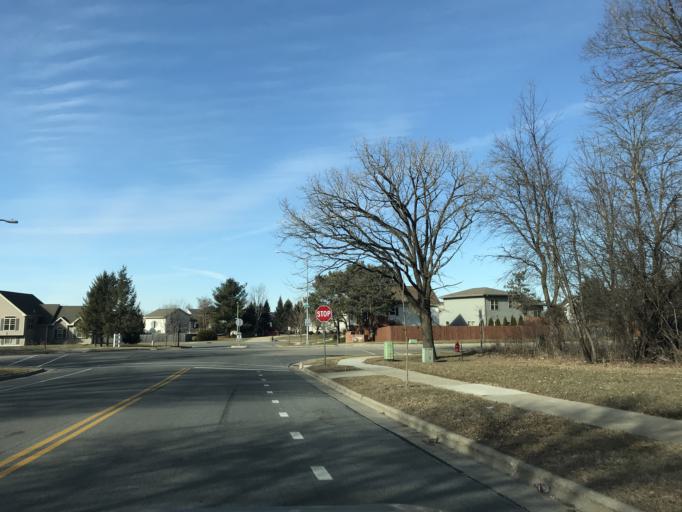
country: US
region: Wisconsin
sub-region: Dane County
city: Maple Bluff
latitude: 43.1426
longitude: -89.3058
